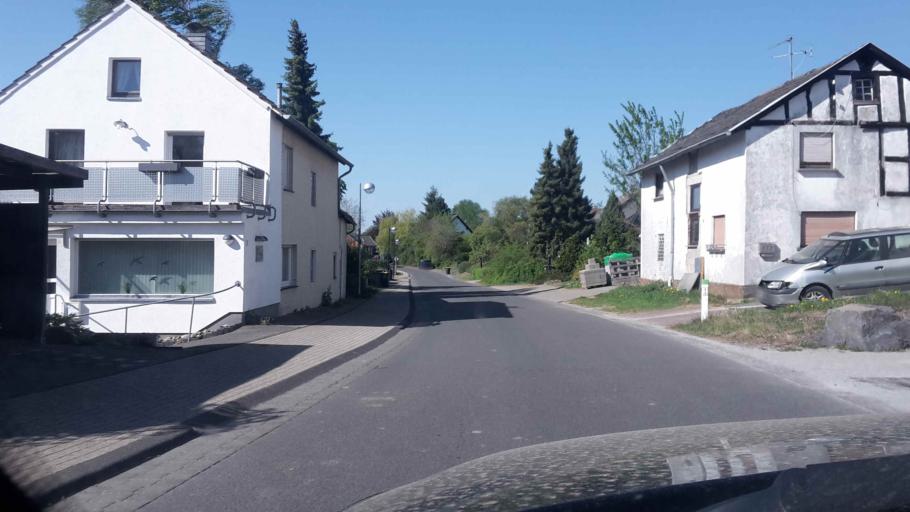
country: DE
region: Rheinland-Pfalz
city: Windhagen
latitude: 50.6678
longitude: 7.3377
